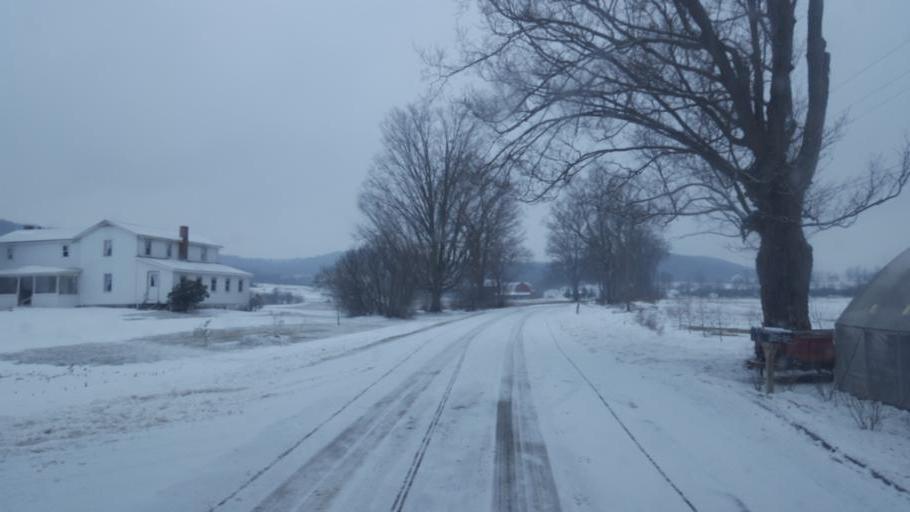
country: US
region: Pennsylvania
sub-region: Tioga County
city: Elkland
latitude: 42.1019
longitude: -77.4560
